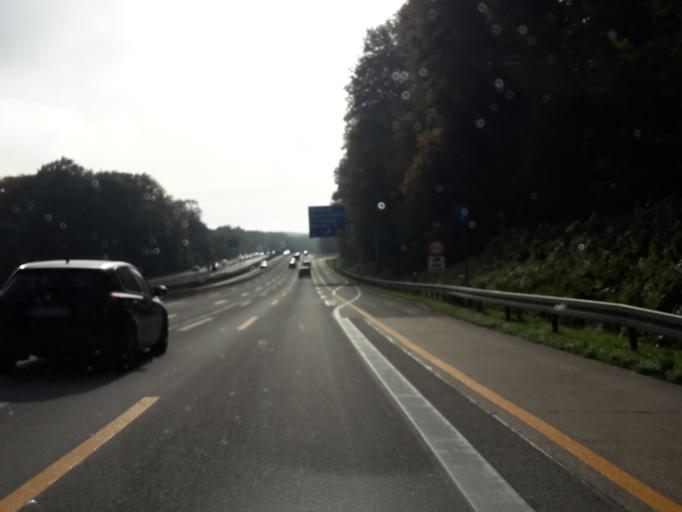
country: DE
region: Hesse
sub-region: Regierungsbezirk Darmstadt
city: Niedernhausen
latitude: 50.1472
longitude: 8.3236
